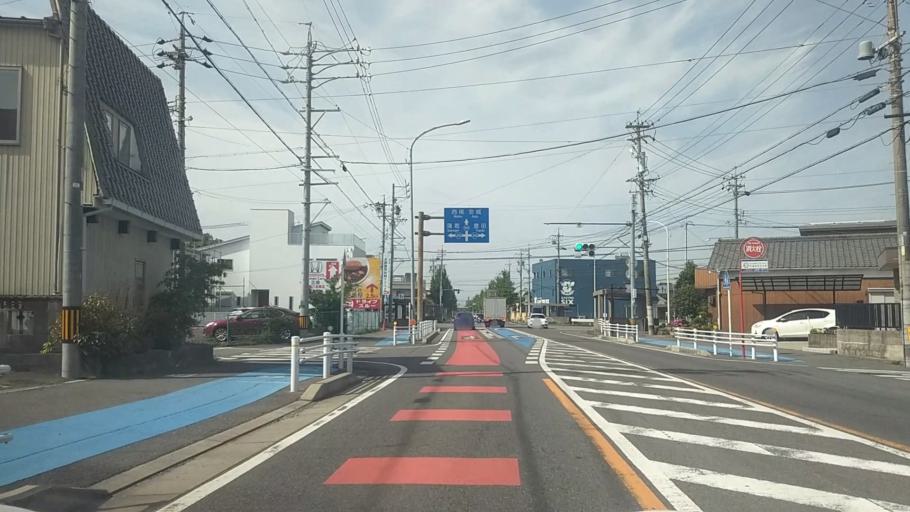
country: JP
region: Aichi
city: Okazaki
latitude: 34.9468
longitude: 137.1559
